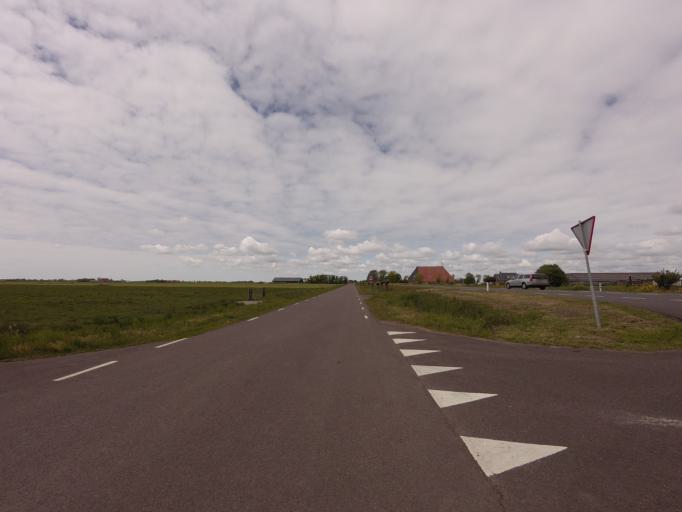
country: NL
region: Friesland
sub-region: Sudwest Fryslan
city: Woudsend
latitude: 52.9489
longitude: 5.6537
